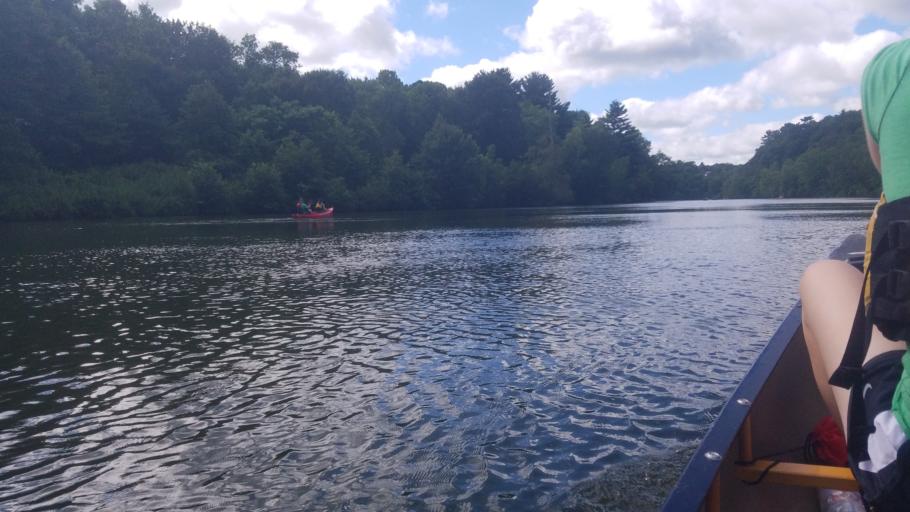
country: US
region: Wisconsin
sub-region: Dunn County
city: Menomonie
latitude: 44.8708
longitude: -91.9421
